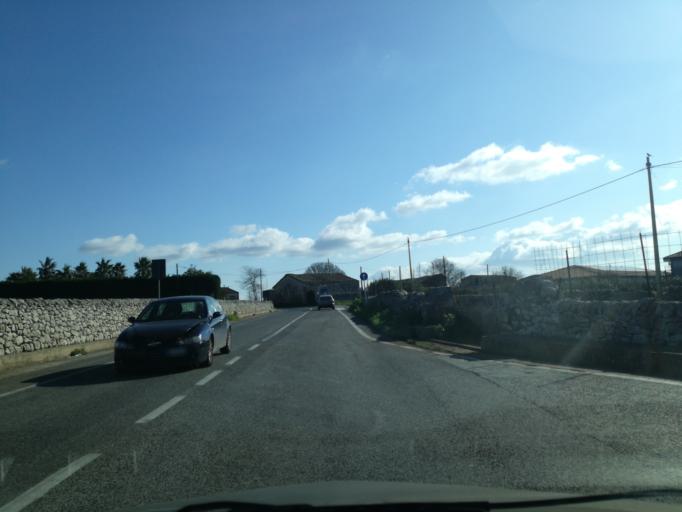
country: IT
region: Sicily
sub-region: Ragusa
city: Comiso
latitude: 36.9404
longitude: 14.6440
